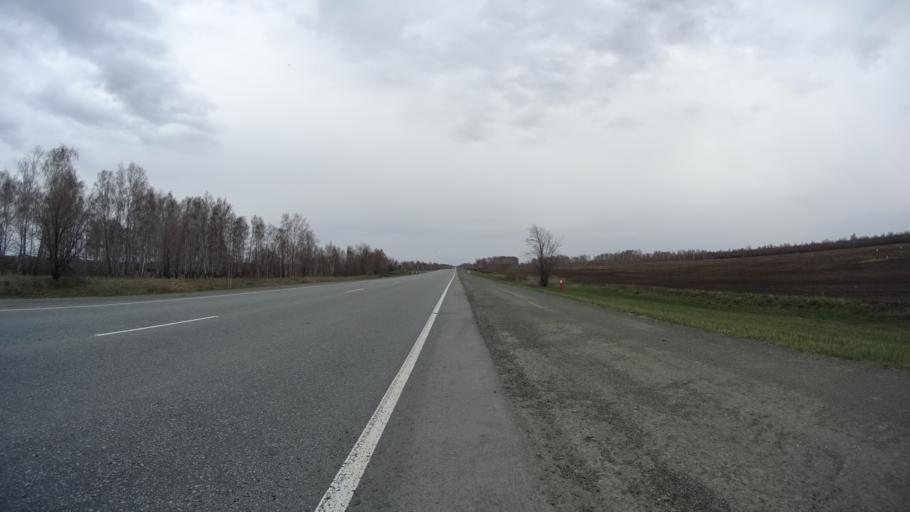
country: RU
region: Chelyabinsk
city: Krasnogorskiy
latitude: 54.6594
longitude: 61.2555
